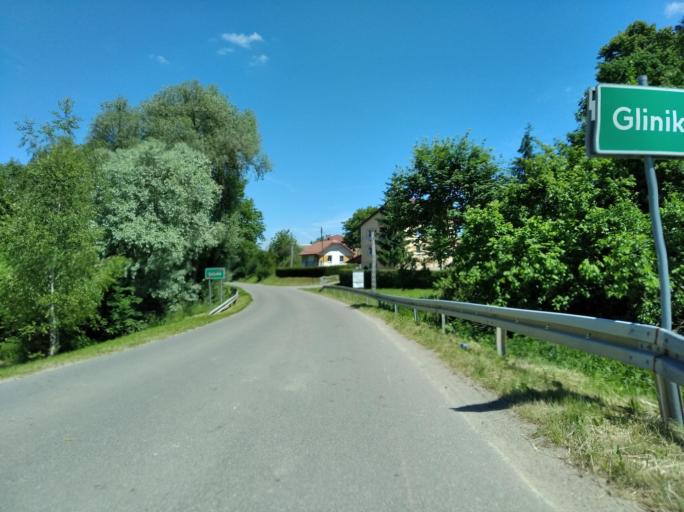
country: PL
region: Subcarpathian Voivodeship
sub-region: Powiat jasielski
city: Tarnowiec
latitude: 49.6857
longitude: 21.5454
